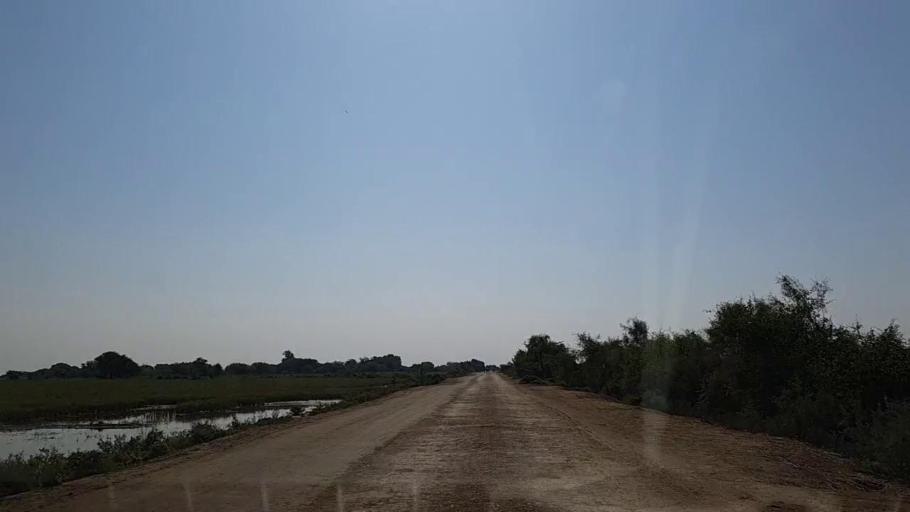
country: PK
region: Sindh
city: Chuhar Jamali
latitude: 24.5179
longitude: 68.0945
